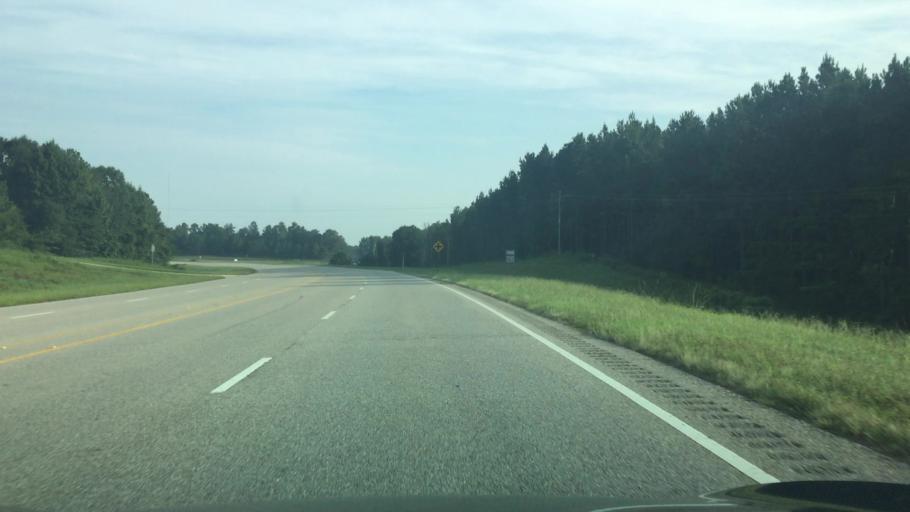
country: US
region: Alabama
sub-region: Covington County
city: Andalusia
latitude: 31.4397
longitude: -86.6119
